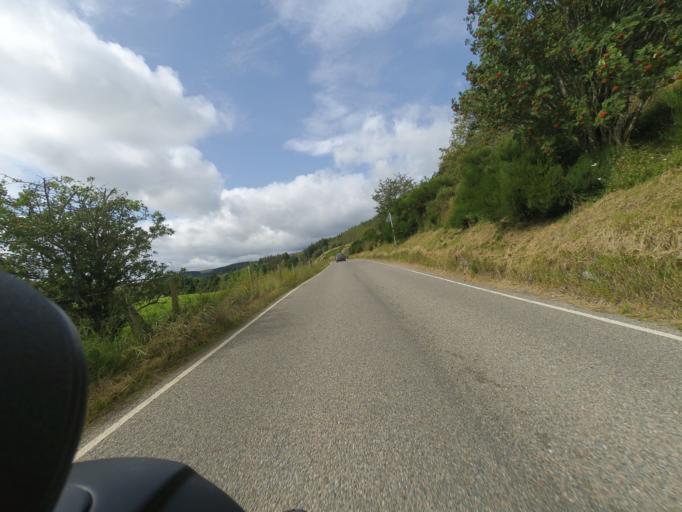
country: GB
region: Scotland
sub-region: Highland
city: Grantown on Spey
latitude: 57.2579
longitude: -3.3892
